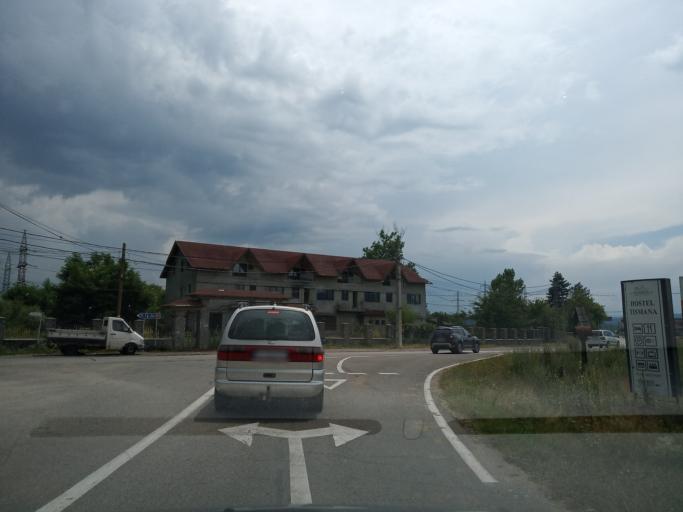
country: RO
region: Gorj
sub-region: Comuna Tismana
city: Tismana
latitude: 45.0392
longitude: 22.9519
